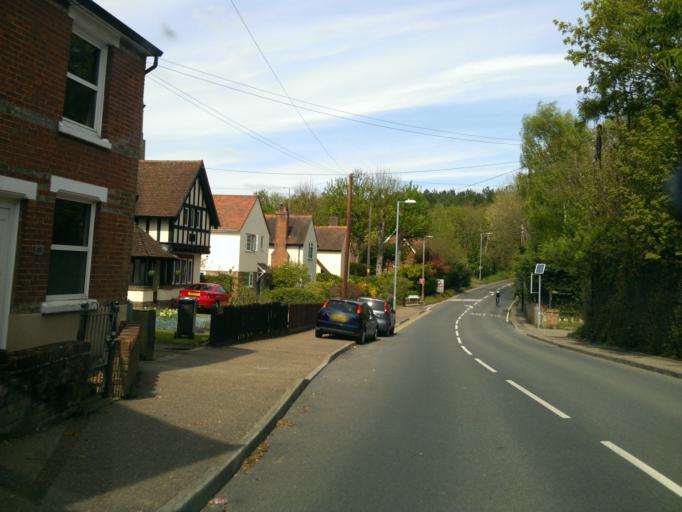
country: GB
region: England
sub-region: Essex
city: Sible Hedingham
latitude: 51.9500
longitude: 0.6370
